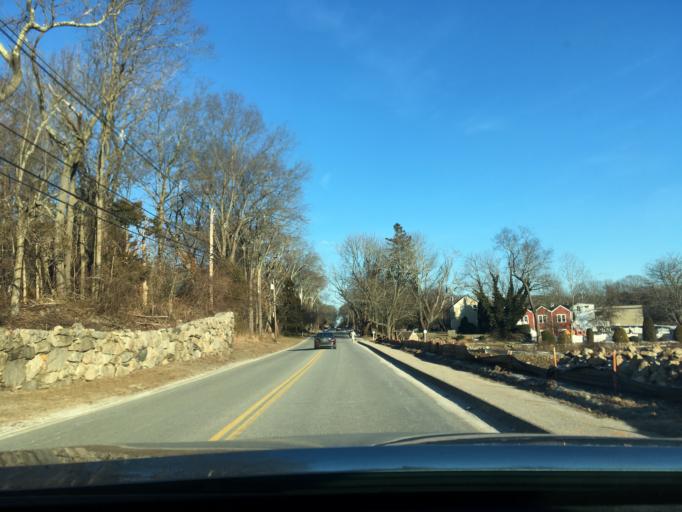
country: US
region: Rhode Island
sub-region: Kent County
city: East Greenwich
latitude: 41.6457
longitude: -71.4920
